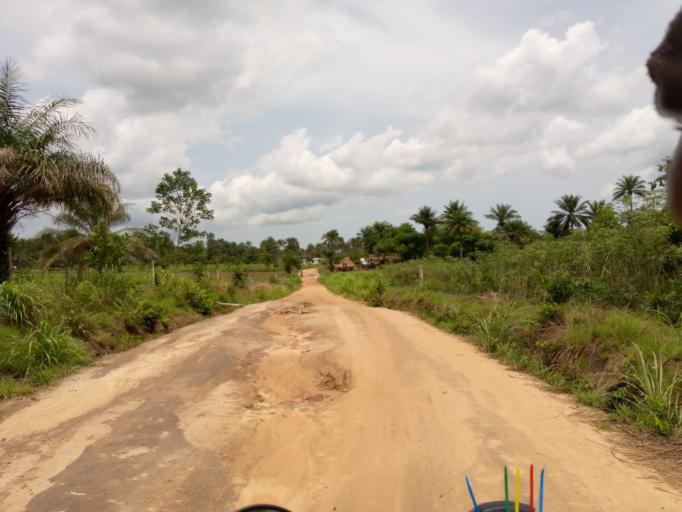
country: SL
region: Western Area
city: Waterloo
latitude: 8.3223
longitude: -12.9408
